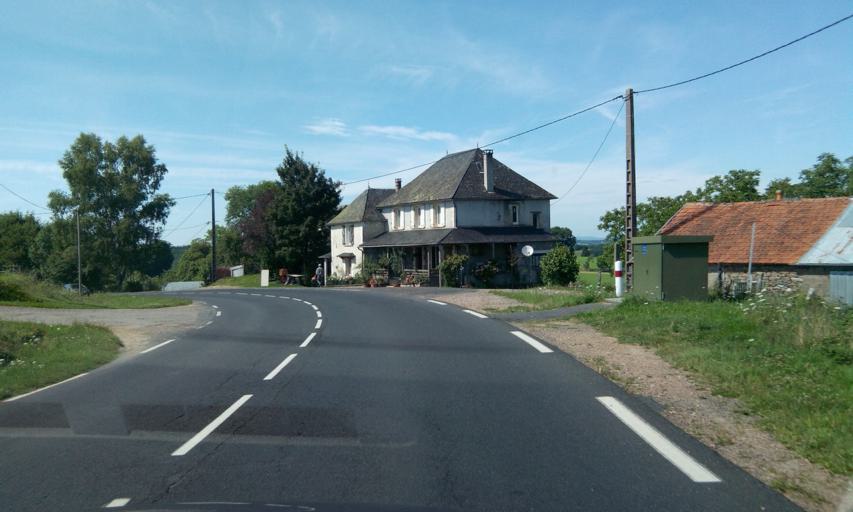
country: FR
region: Limousin
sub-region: Departement de la Correze
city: Beynat
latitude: 45.1258
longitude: 1.7867
